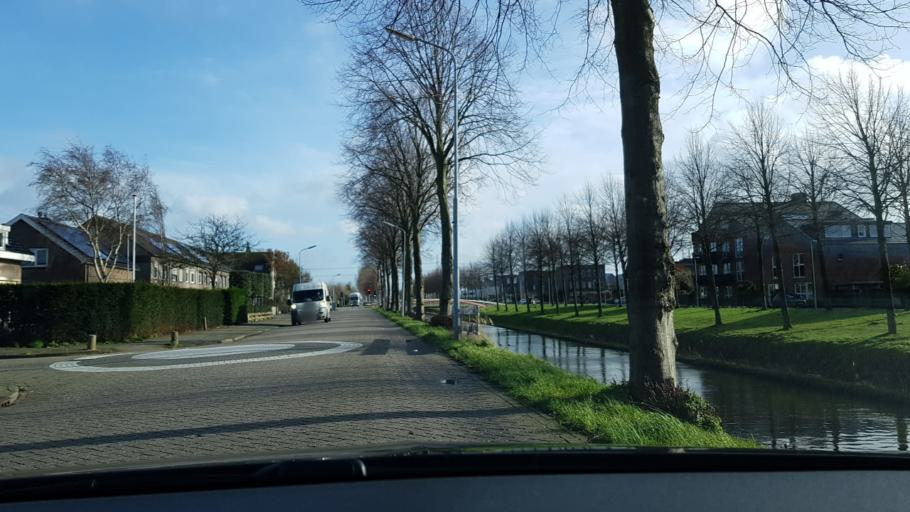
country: NL
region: North Holland
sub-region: Gemeente Haarlemmermeer
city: Hoofddorp
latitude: 52.3494
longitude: 4.6785
